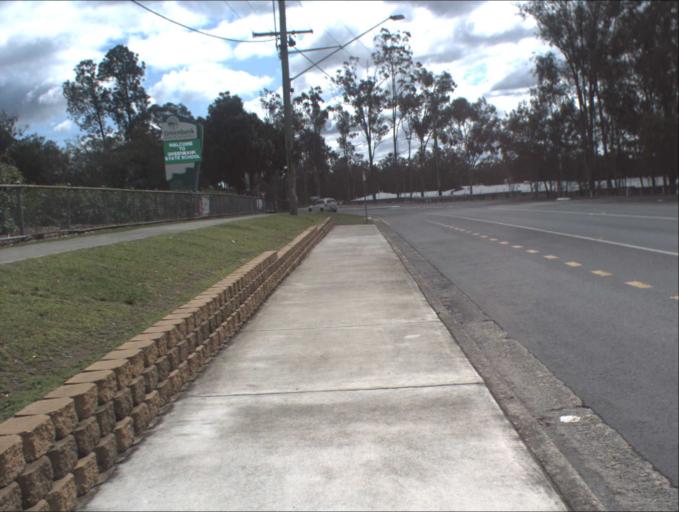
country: AU
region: Queensland
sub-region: Logan
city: Park Ridge South
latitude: -27.7109
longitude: 152.9777
